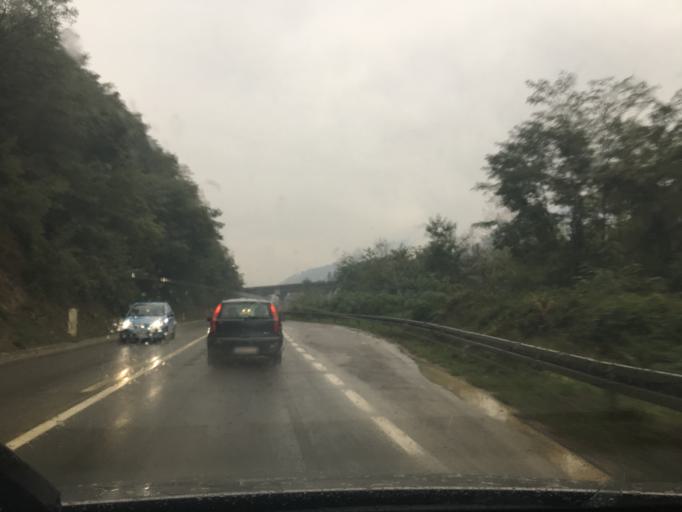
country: RS
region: Central Serbia
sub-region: Pcinjski Okrug
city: Vladicin Han
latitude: 42.7634
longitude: 22.0844
